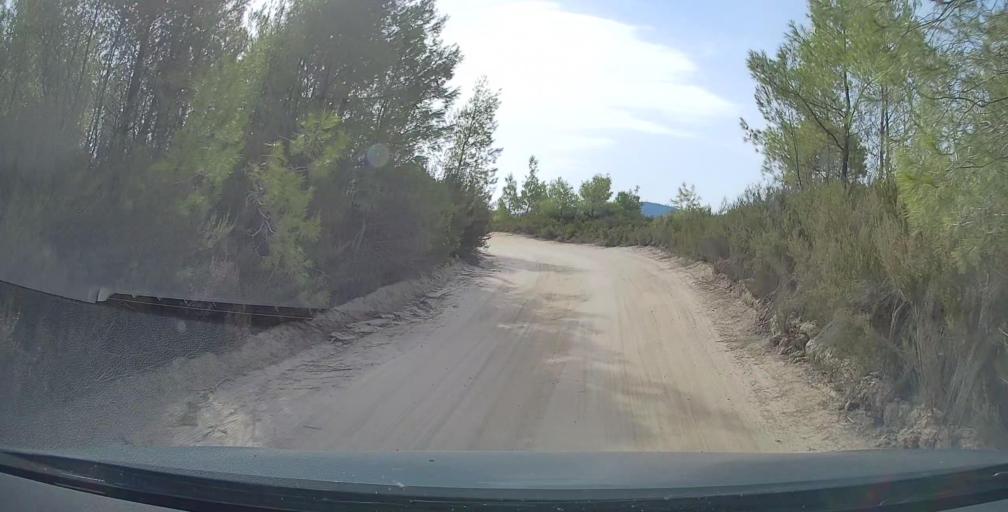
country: GR
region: Central Macedonia
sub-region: Nomos Chalkidikis
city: Sarti
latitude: 40.1295
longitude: 23.9551
